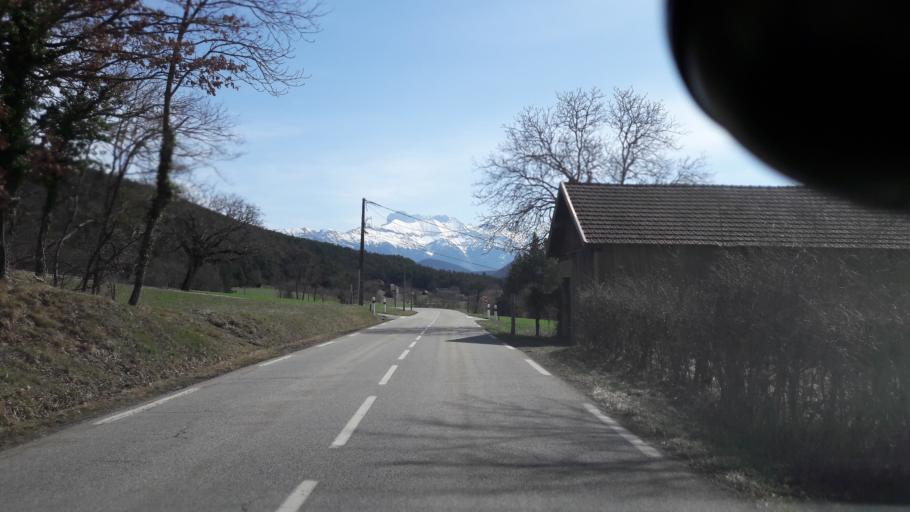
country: FR
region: Rhone-Alpes
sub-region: Departement de l'Isere
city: La Motte-Saint-Martin
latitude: 44.8855
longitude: 5.6419
